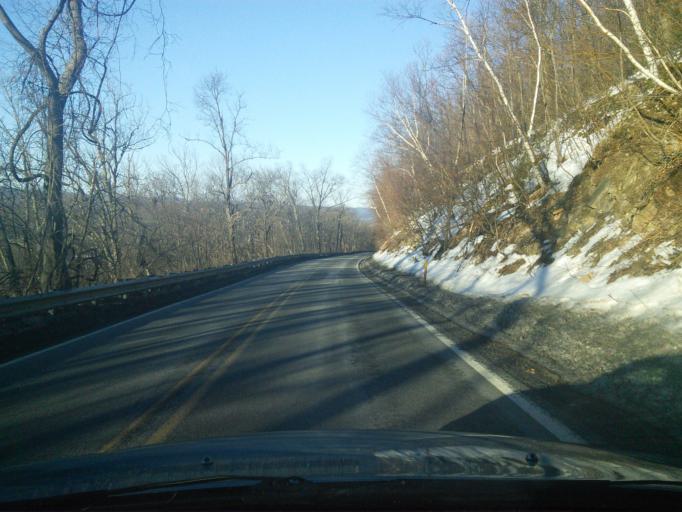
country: US
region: Pennsylvania
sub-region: Centre County
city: Park Forest Village
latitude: 40.8455
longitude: -77.9510
